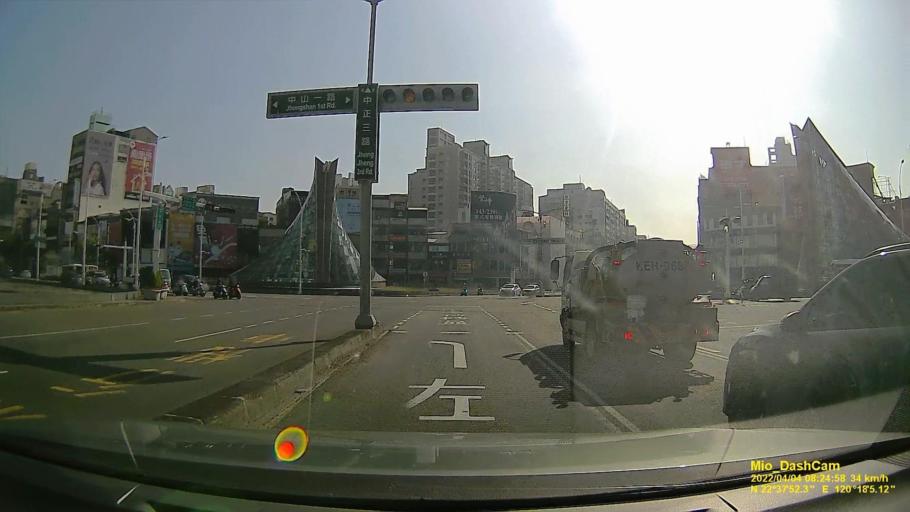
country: TW
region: Kaohsiung
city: Kaohsiung
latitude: 22.6312
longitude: 120.3015
